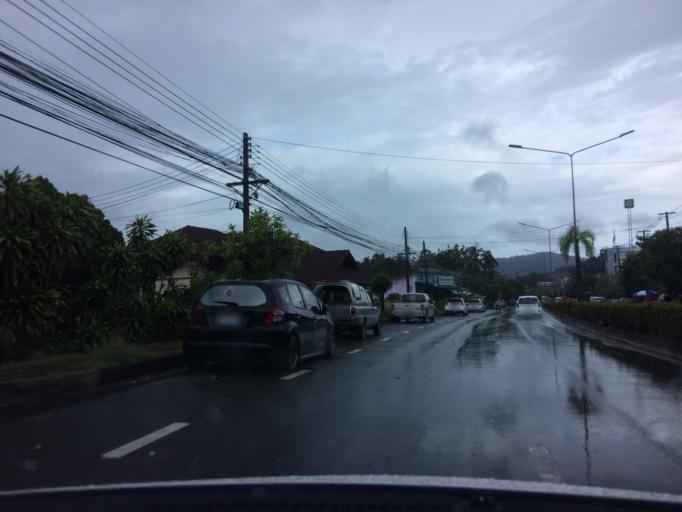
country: TH
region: Phuket
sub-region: Amphoe Kathu
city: Kathu
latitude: 7.9153
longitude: 98.3321
